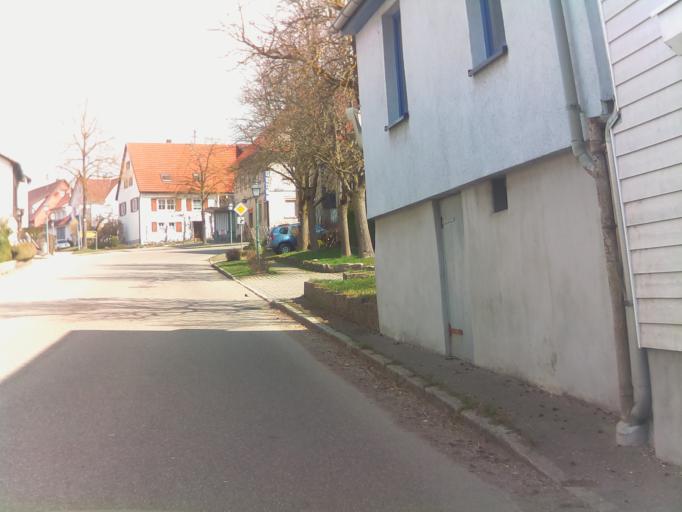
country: DE
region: Baden-Wuerttemberg
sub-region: Tuebingen Region
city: Bad Urach
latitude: 48.4559
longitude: 9.3893
